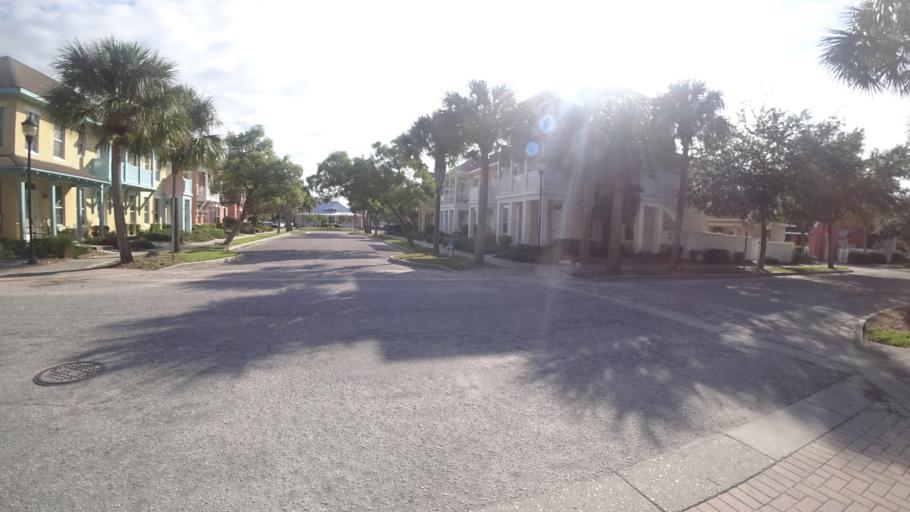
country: US
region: Florida
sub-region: Manatee County
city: Bradenton
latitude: 27.4861
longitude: -82.5648
